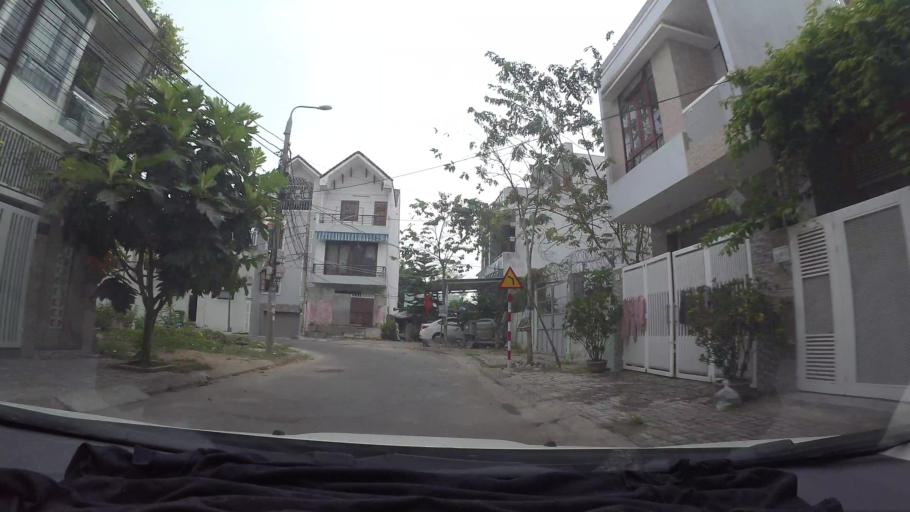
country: VN
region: Da Nang
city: Cam Le
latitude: 16.0263
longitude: 108.2221
